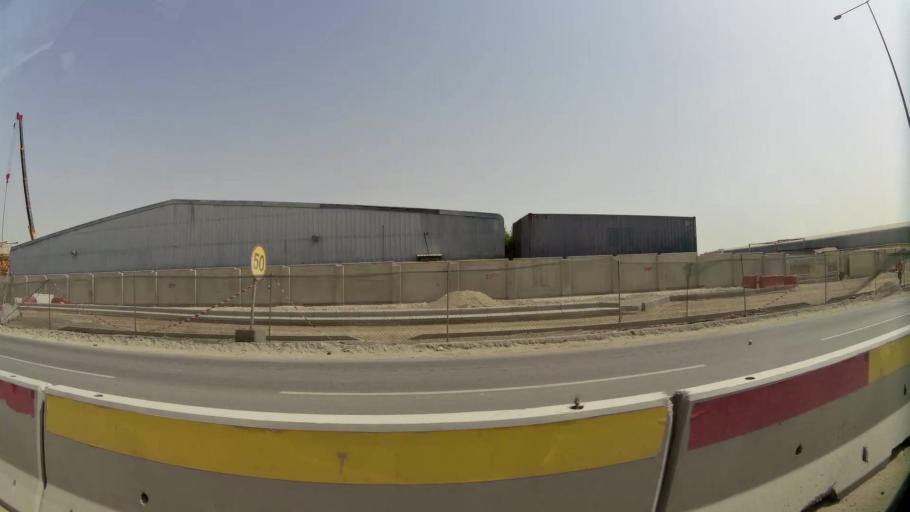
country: QA
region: Baladiyat ar Rayyan
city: Ar Rayyan
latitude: 25.1846
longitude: 51.4238
